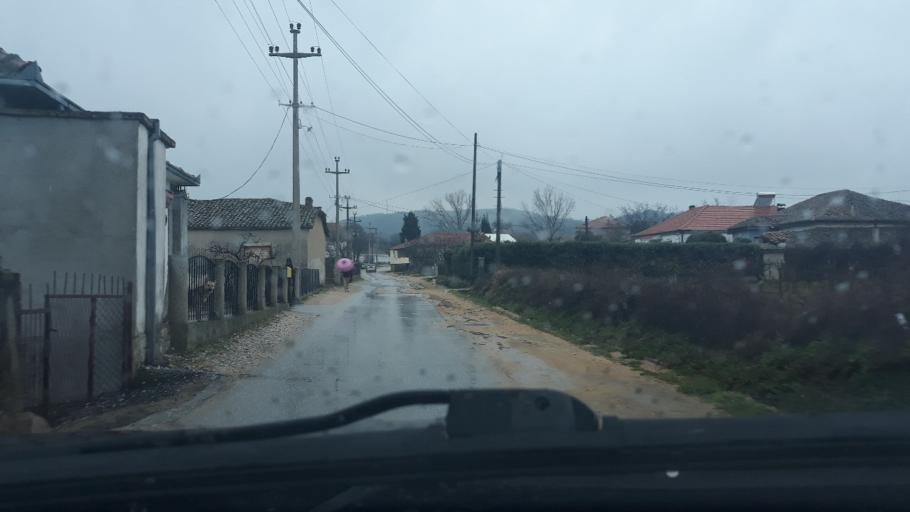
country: MK
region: Bogdanci
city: Bogdanci
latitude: 41.2432
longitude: 22.6129
